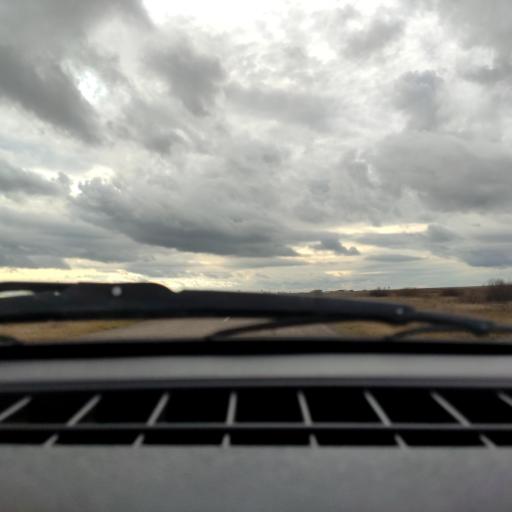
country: RU
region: Bashkortostan
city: Asanovo
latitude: 54.9227
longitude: 55.5123
